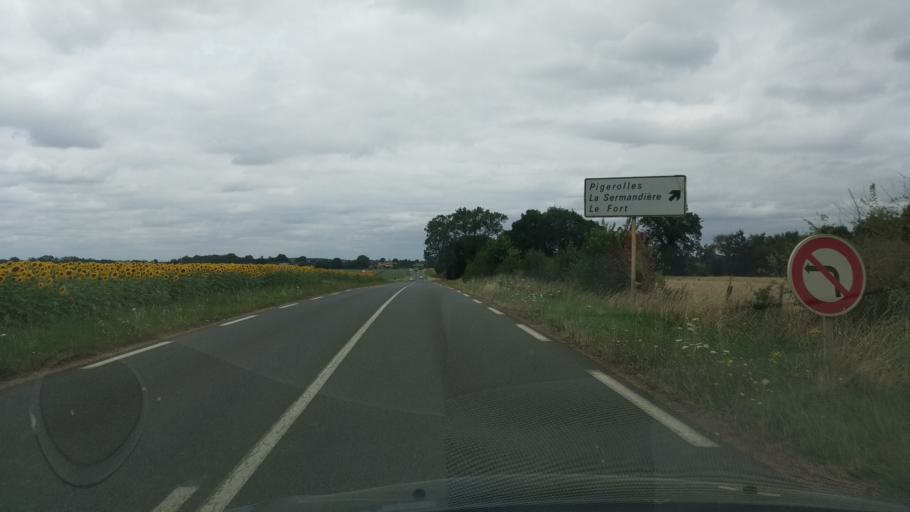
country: FR
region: Poitou-Charentes
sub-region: Departement de la Vienne
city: La Villedieu-du-Clain
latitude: 46.4324
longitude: 0.3752
